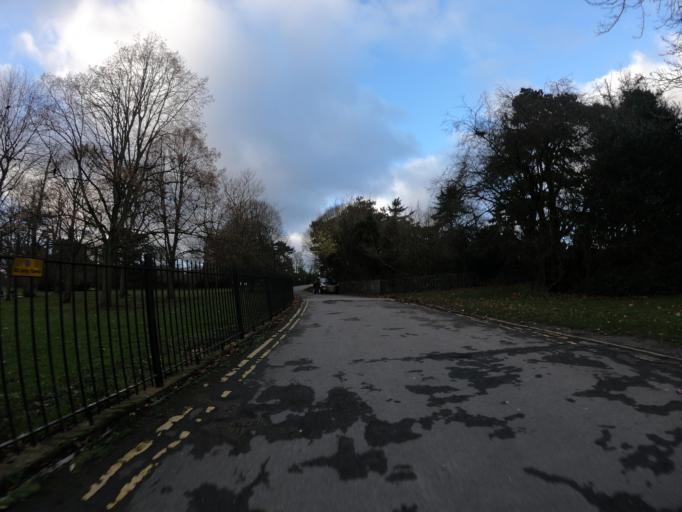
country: GB
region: England
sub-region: Greater London
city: Welling
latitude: 51.4500
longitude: 0.0800
